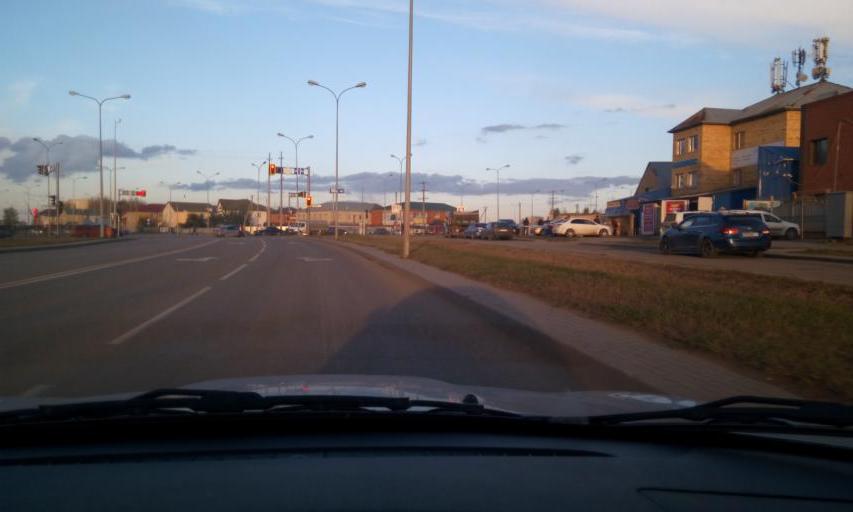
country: KZ
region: Astana Qalasy
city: Astana
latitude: 51.1376
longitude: 71.5177
